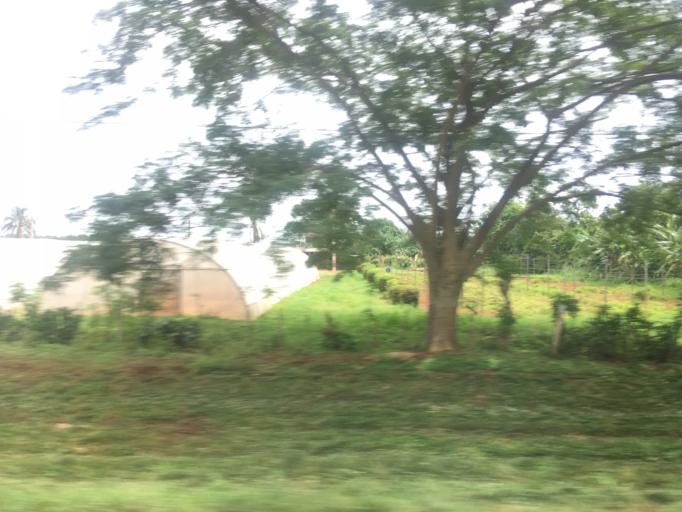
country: CU
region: Matanzas
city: Jovellanos
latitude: 22.7982
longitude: -81.1612
